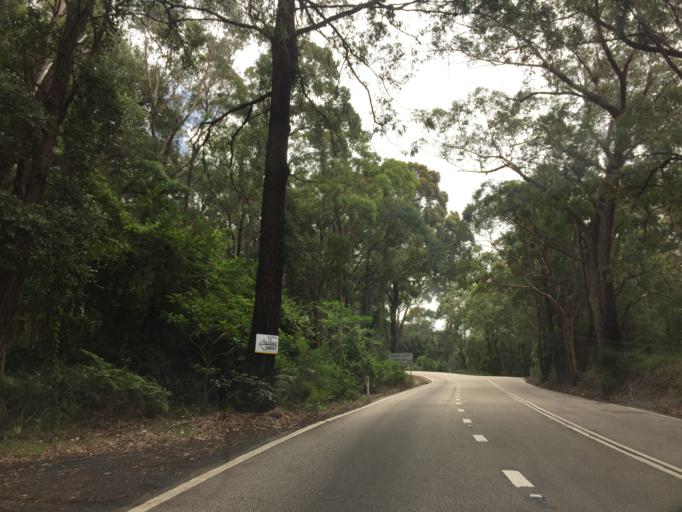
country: AU
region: New South Wales
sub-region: Hawkesbury
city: Richmond
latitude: -33.5417
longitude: 150.6332
